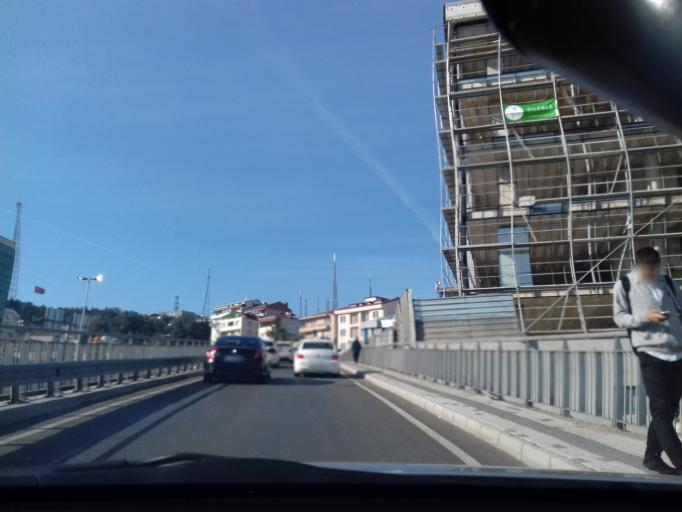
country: TR
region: Istanbul
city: Umraniye
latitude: 41.0218
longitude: 29.0746
